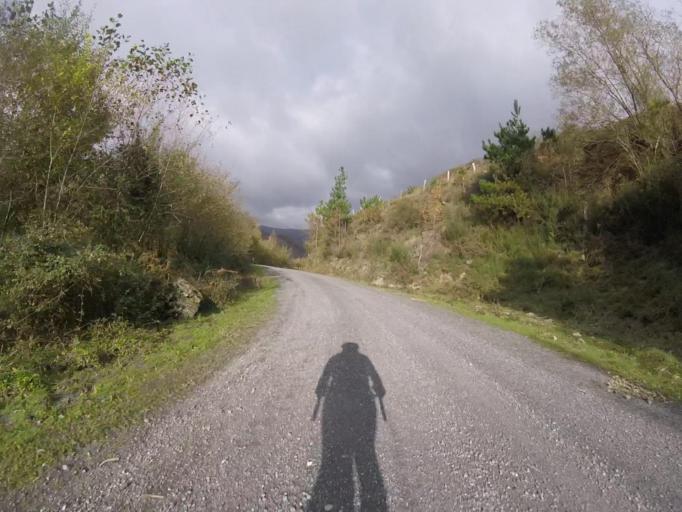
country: ES
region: Navarre
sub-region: Provincia de Navarra
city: Goizueta
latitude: 43.2102
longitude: -1.8318
